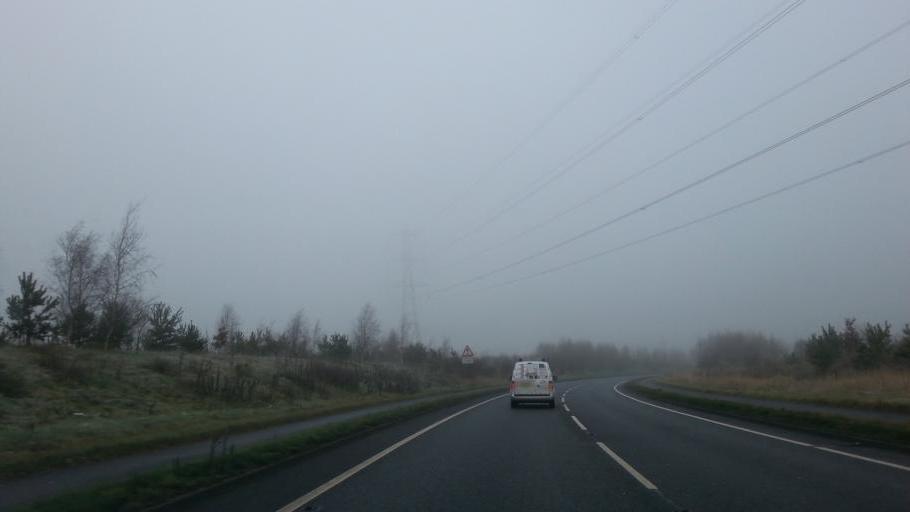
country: GB
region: England
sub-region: Cheshire East
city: Alderley Edge
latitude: 53.2921
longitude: -2.2553
